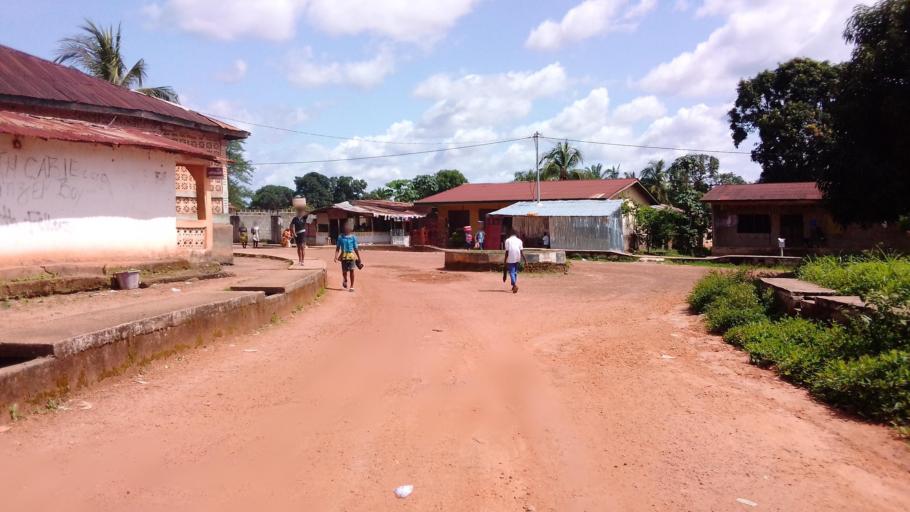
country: SL
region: Northern Province
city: Makeni
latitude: 8.8824
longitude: -12.0409
